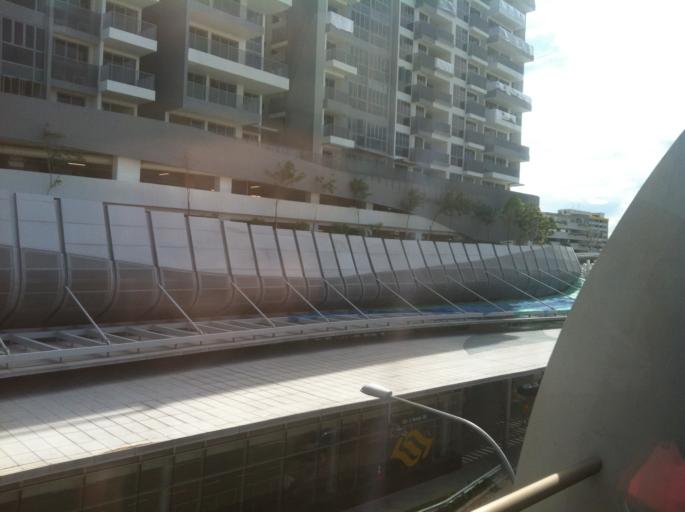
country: SG
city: Singapore
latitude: 1.3240
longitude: 103.9295
